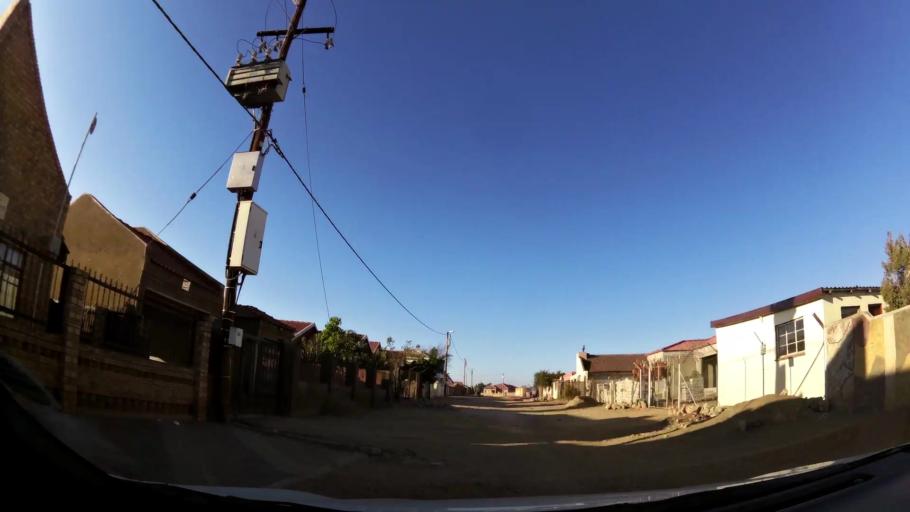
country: ZA
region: Limpopo
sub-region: Capricorn District Municipality
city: Polokwane
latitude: -23.8437
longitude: 29.3579
